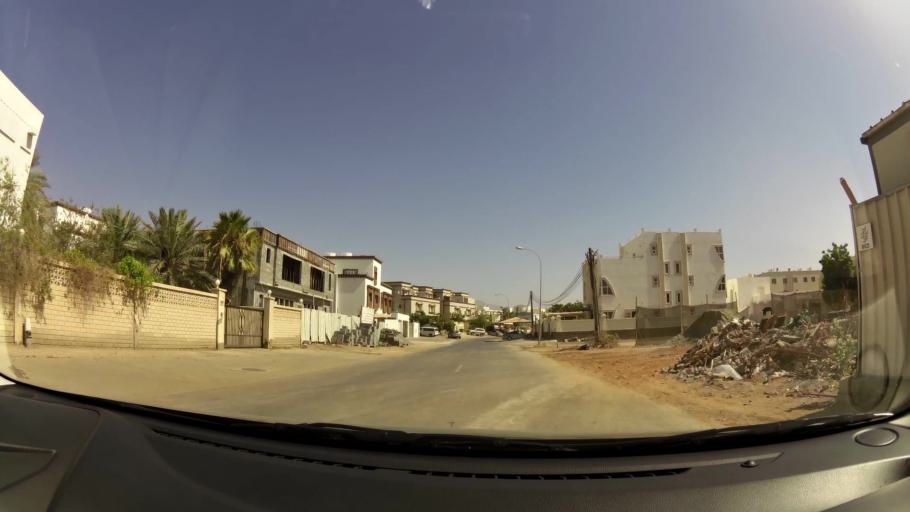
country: OM
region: Muhafazat Masqat
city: Bawshar
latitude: 23.6028
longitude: 58.3832
